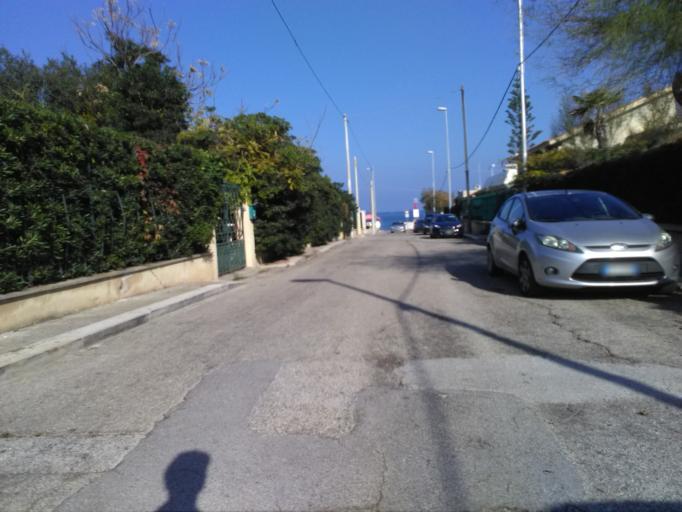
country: IT
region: Apulia
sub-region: Provincia di Bari
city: San Paolo
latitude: 41.1595
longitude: 16.7687
